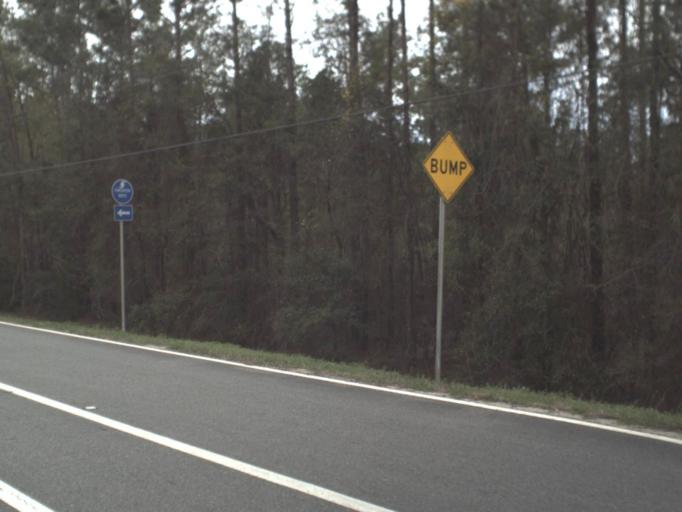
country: US
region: Florida
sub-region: Wakulla County
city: Crawfordville
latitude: 30.2642
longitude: -84.3635
